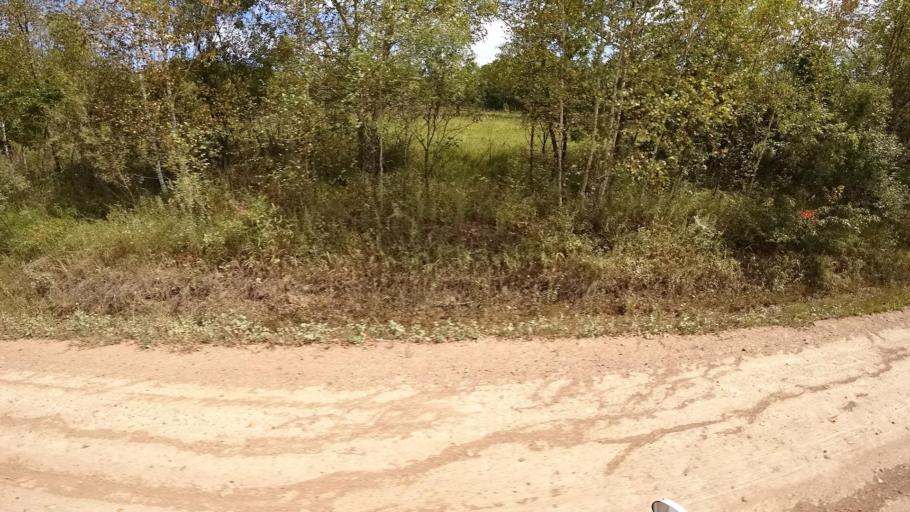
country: RU
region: Primorskiy
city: Yakovlevka
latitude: 44.7286
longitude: 133.6097
